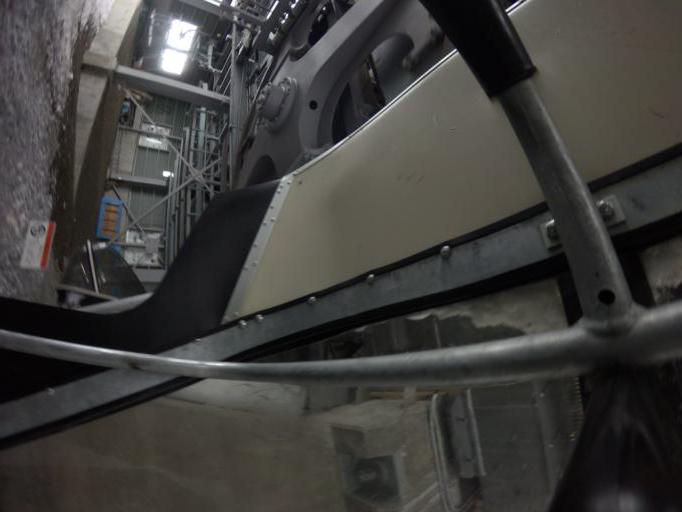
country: JP
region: Hokkaido
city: Sapporo
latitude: 43.0841
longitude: 141.2044
